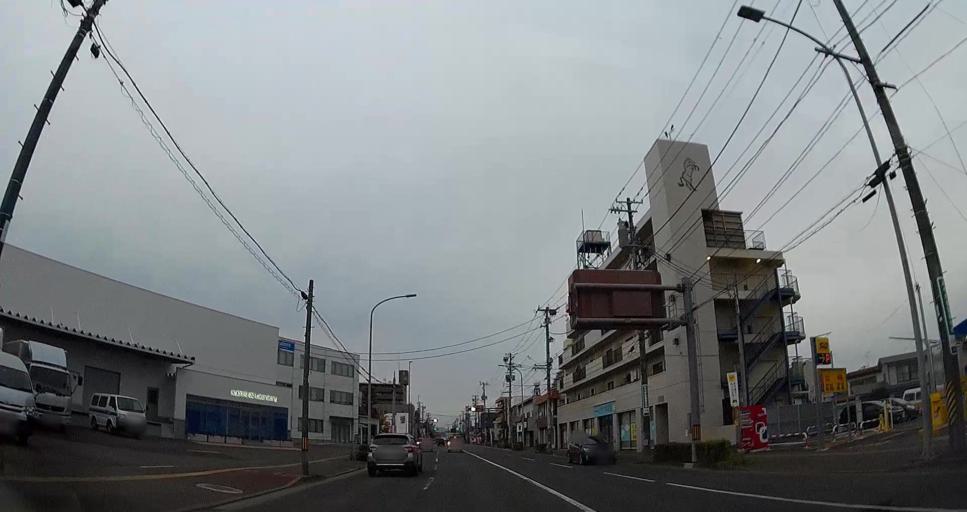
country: JP
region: Miyagi
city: Sendai
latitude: 38.2255
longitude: 140.8966
